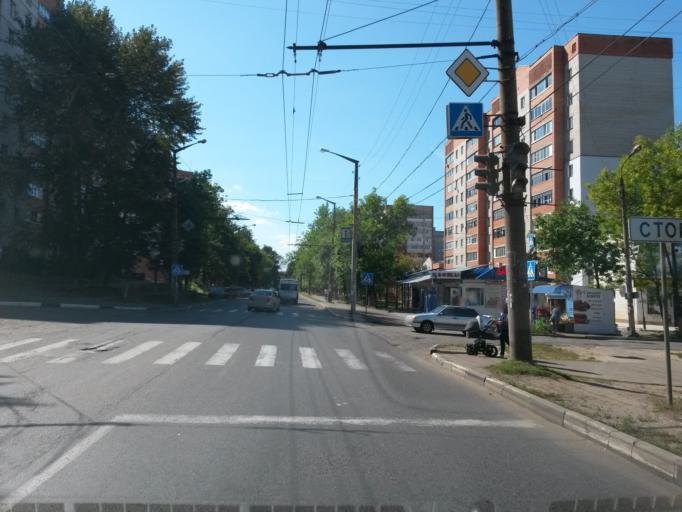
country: RU
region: Jaroslavl
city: Yaroslavl
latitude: 57.5838
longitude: 39.8391
